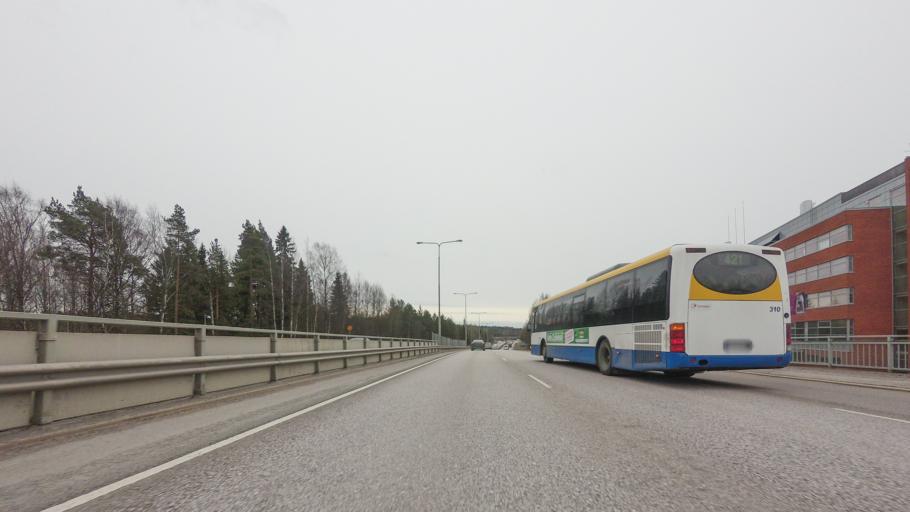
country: FI
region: Uusimaa
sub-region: Helsinki
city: Helsinki
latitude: 60.2272
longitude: 24.9070
